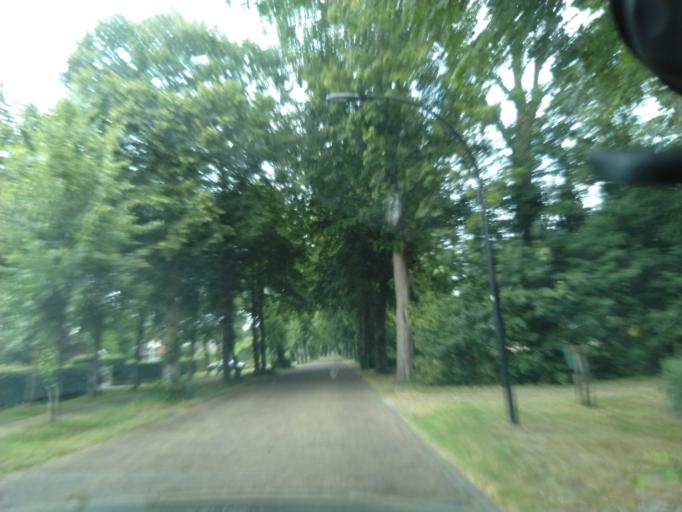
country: NL
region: Groningen
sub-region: Gemeente Vlagtwedde
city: Vlagtwedde
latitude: 53.0873
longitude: 7.1341
